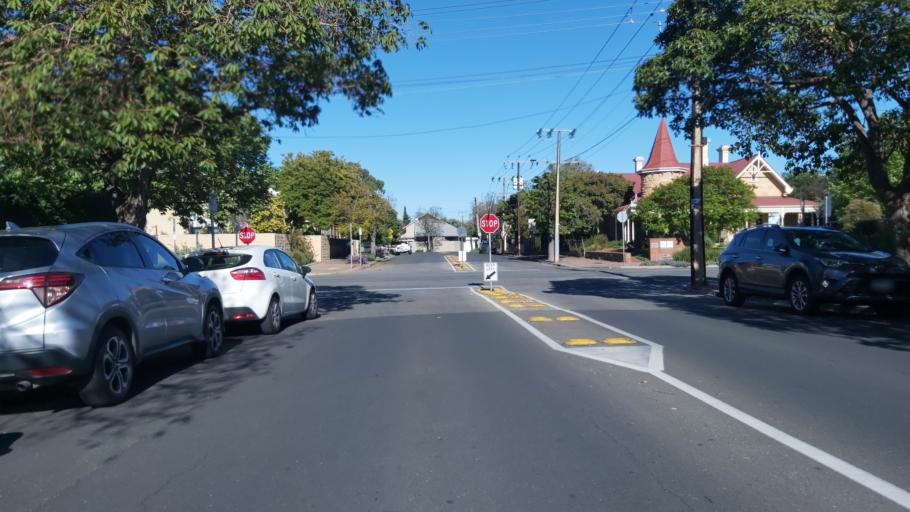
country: AU
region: South Australia
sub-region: Unley
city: Unley
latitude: -34.9450
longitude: 138.5997
